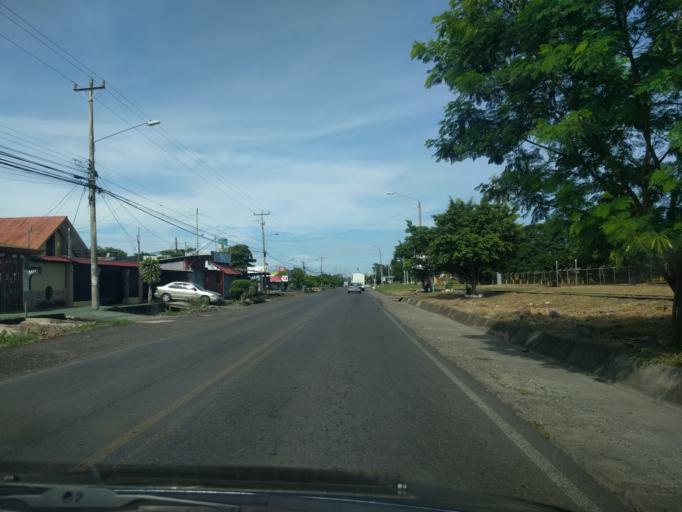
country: CR
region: Puntarenas
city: Esparza
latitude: 9.9840
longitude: -84.7192
